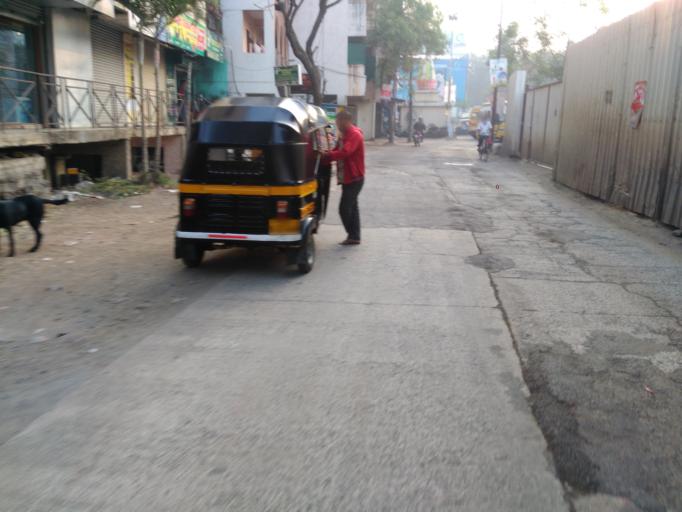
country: IN
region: Maharashtra
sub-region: Pune Division
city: Pune
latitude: 18.4590
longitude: 73.9116
